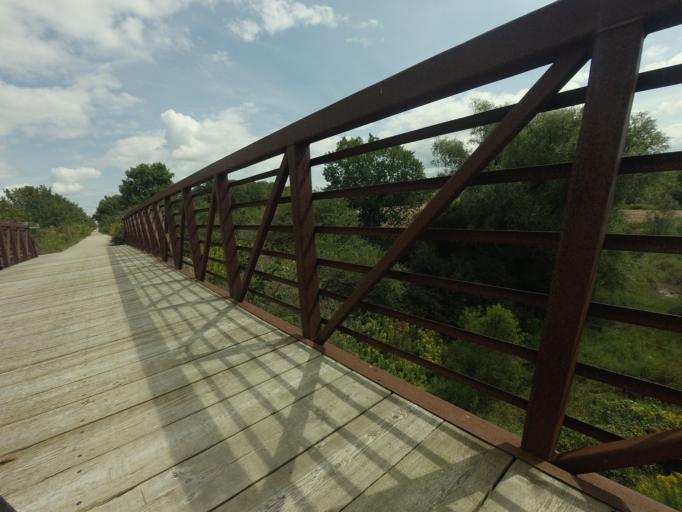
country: CA
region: Ontario
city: North Perth
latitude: 43.5750
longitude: -80.8240
